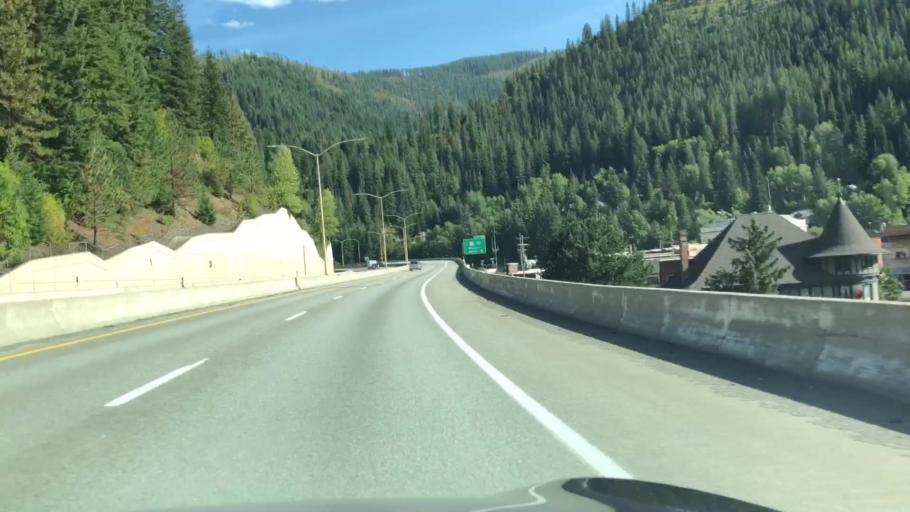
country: US
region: Idaho
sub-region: Shoshone County
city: Wallace
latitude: 47.4739
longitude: -115.9239
